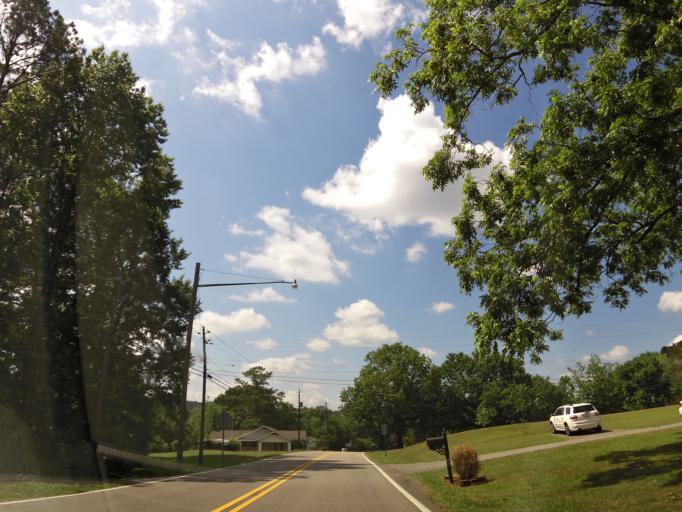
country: US
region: Alabama
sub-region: Marion County
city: Guin
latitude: 33.9691
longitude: -87.9076
